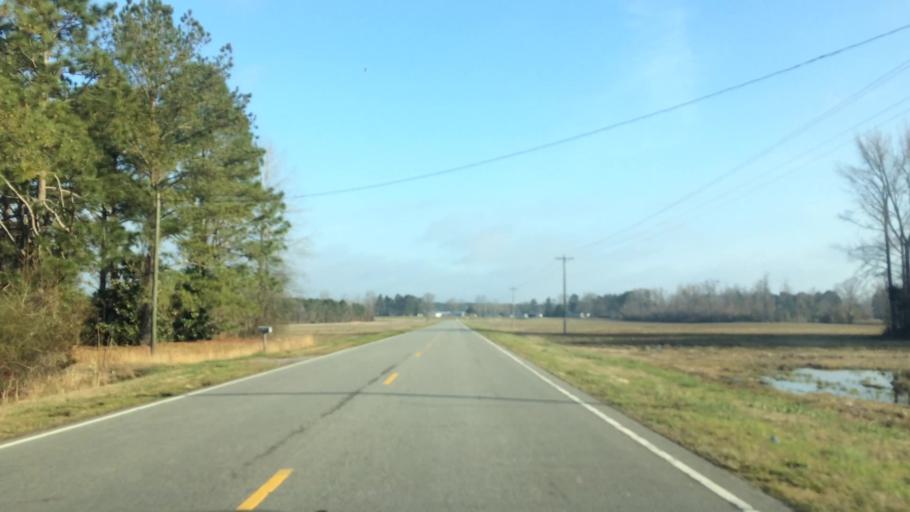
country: US
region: North Carolina
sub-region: Edgecombe County
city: Pinetops
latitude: 35.7228
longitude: -77.6348
